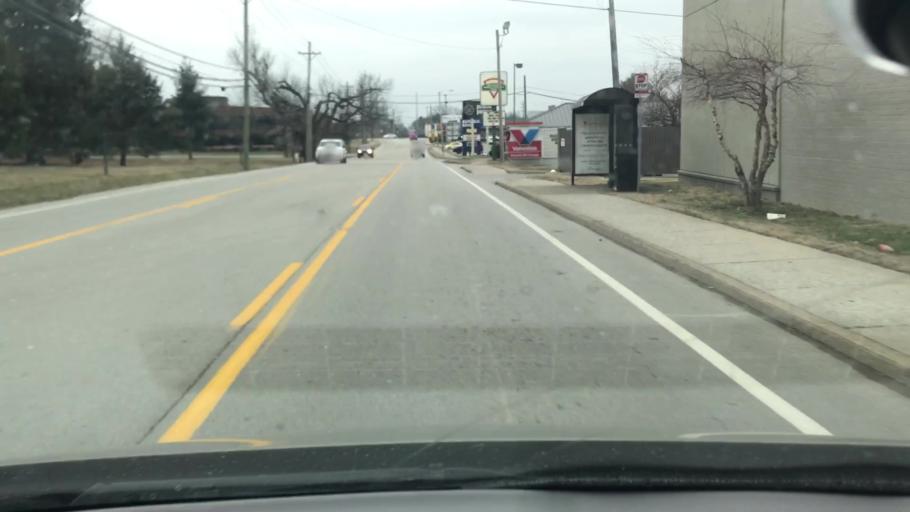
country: US
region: Kentucky
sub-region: Jefferson County
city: Windy Hills
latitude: 38.2822
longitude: -85.6312
